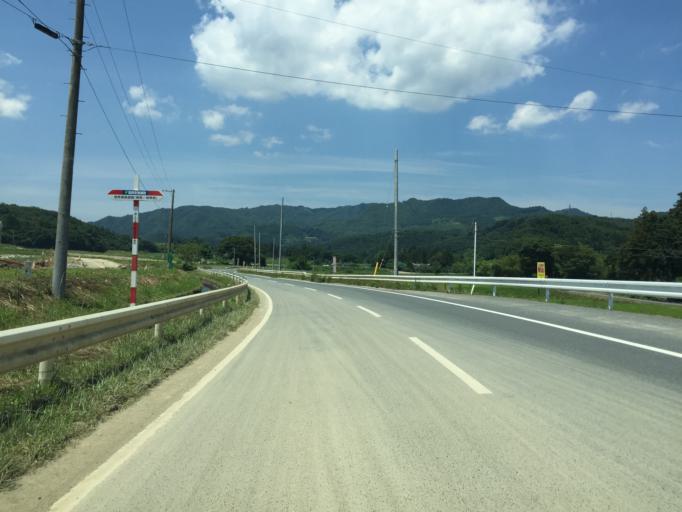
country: JP
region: Miyagi
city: Marumori
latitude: 37.7735
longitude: 140.8922
